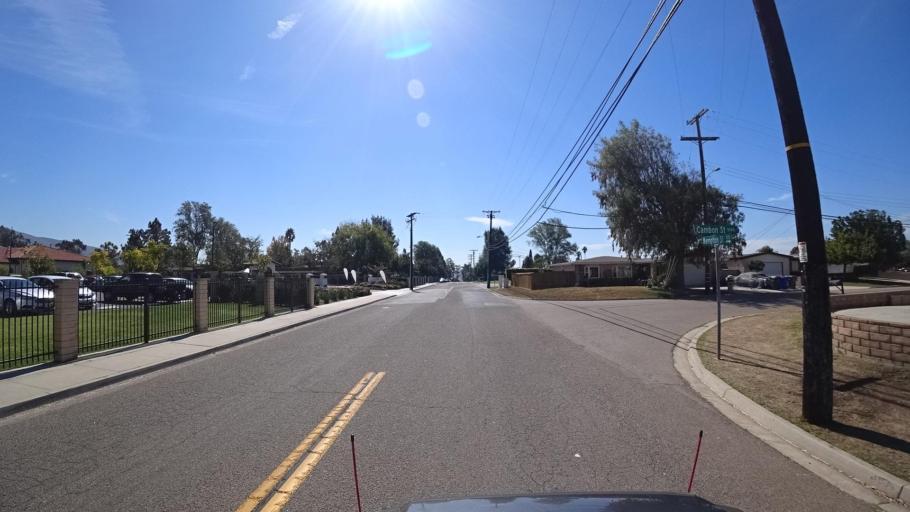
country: US
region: California
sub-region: San Diego County
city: La Presa
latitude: 32.7031
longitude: -117.0020
